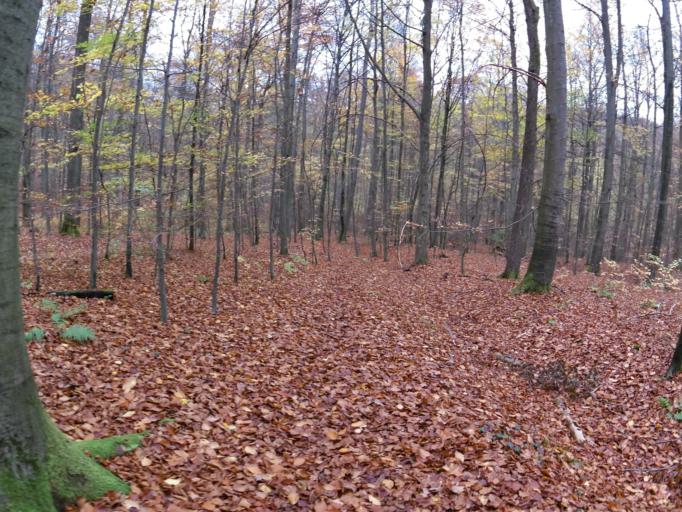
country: DE
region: Thuringia
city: Bischofroda
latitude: 51.0780
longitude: 10.3787
